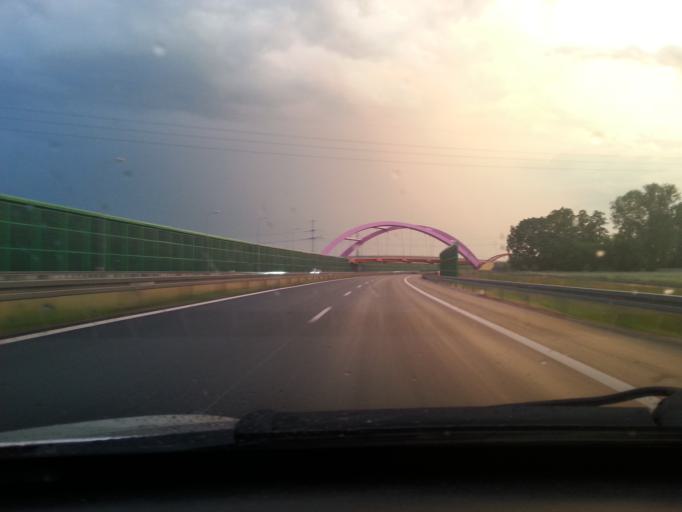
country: PL
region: Lodz Voivodeship
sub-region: Powiat pabianicki
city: Pabianice
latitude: 51.6874
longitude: 19.3393
